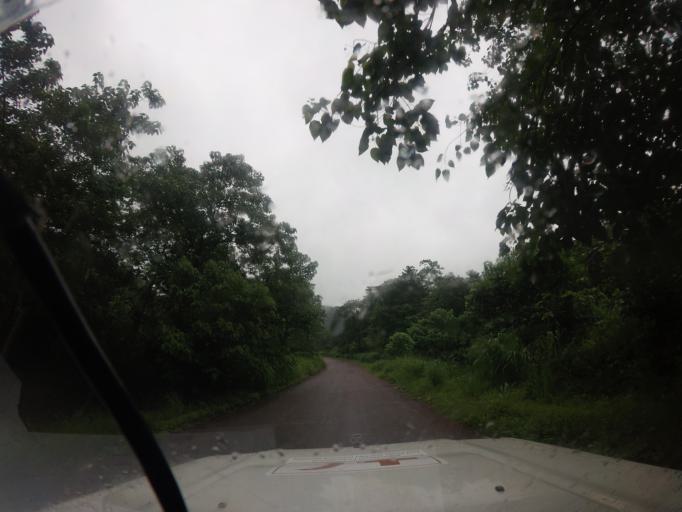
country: SL
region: Northern Province
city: Kabala
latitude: 9.4567
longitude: -11.6992
